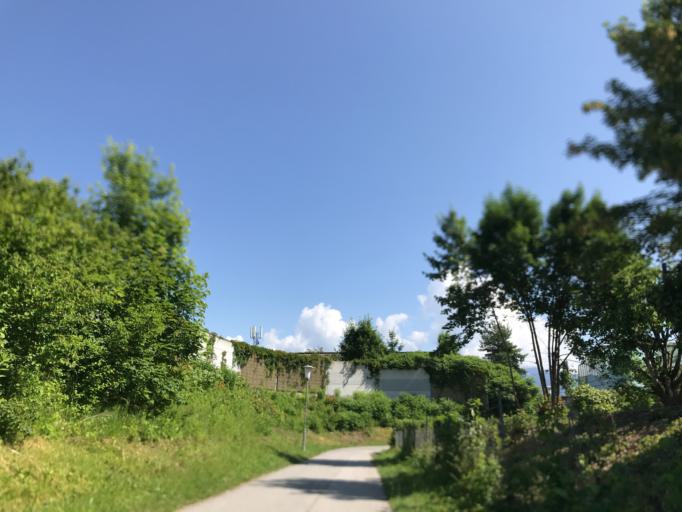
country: AT
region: Carinthia
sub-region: Villach Stadt
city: Villach
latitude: 46.5890
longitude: 13.8294
